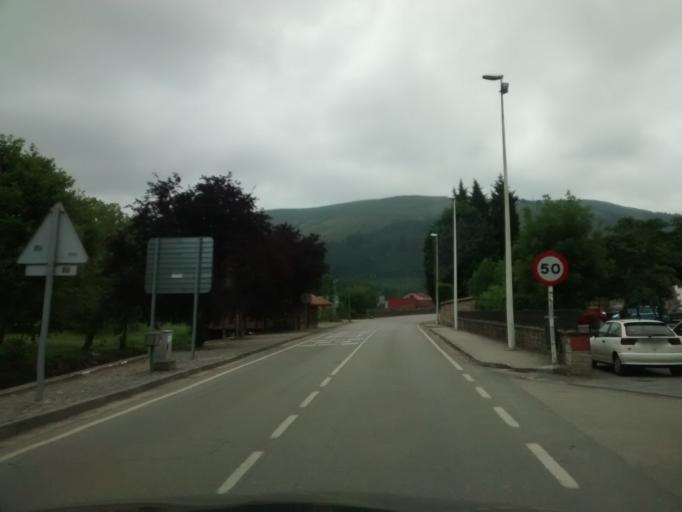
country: ES
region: Cantabria
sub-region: Provincia de Cantabria
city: Cabezon de la Sal
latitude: 43.2935
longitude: -4.2365
